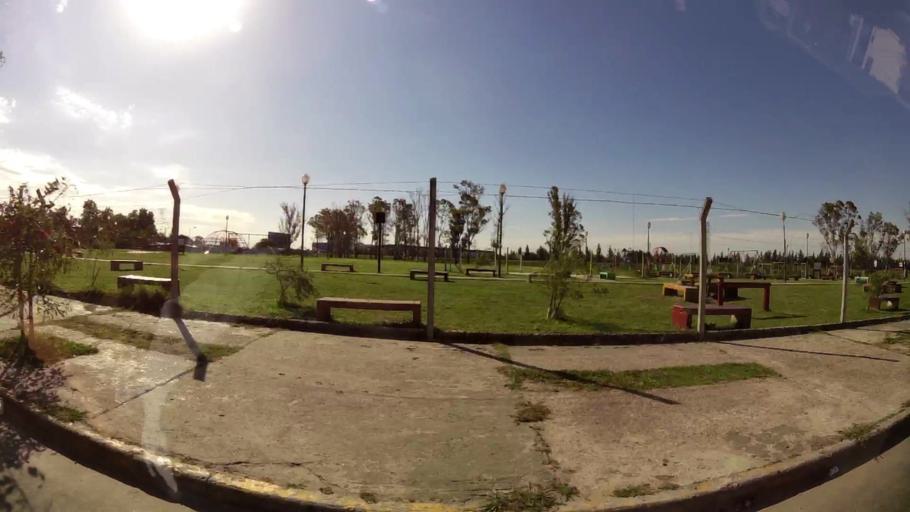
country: AR
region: Buenos Aires
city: Hurlingham
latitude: -34.5527
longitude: -58.6100
